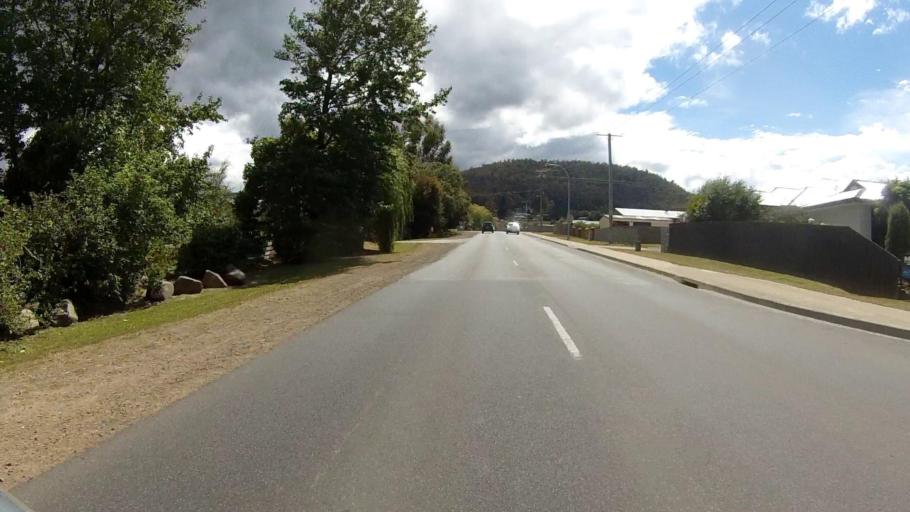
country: AU
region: Tasmania
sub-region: Huon Valley
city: Huonville
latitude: -43.0123
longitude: 147.0392
